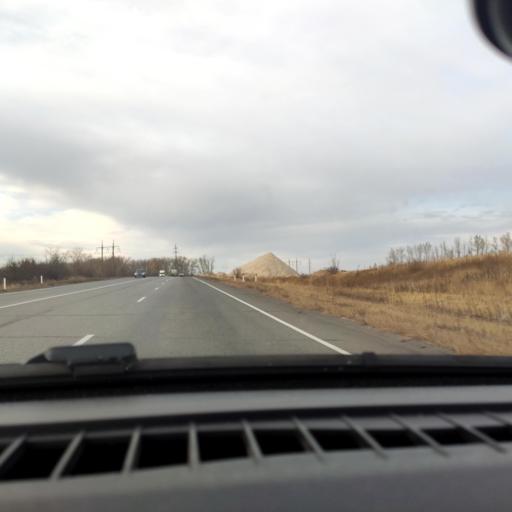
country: RU
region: Voronezj
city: Ostrogozhsk
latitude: 50.9424
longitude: 39.0551
